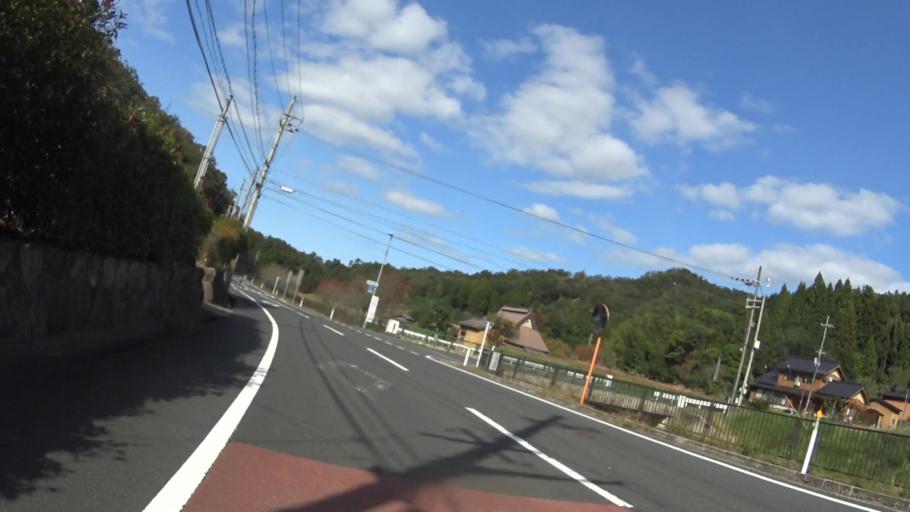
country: JP
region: Hyogo
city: Toyooka
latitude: 35.5620
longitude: 134.9795
